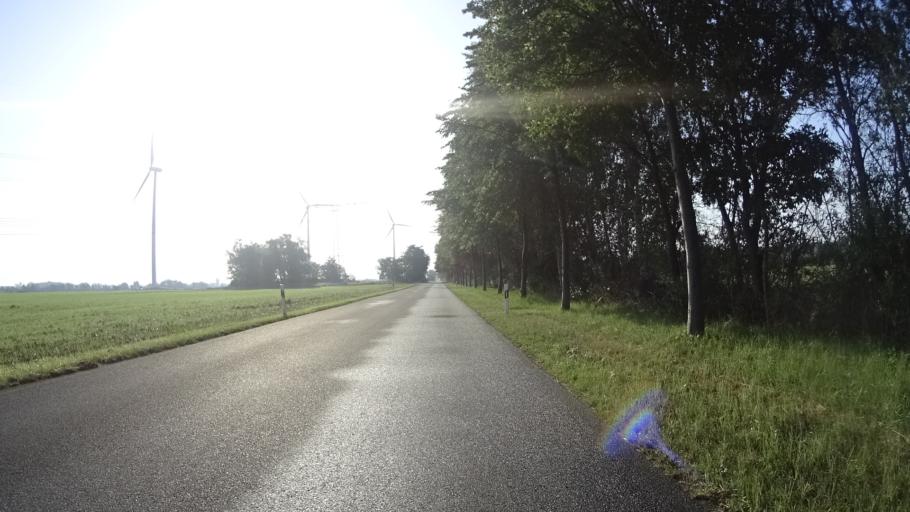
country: DE
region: Brandenburg
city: Kasel-Golzig
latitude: 51.9838
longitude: 13.7220
